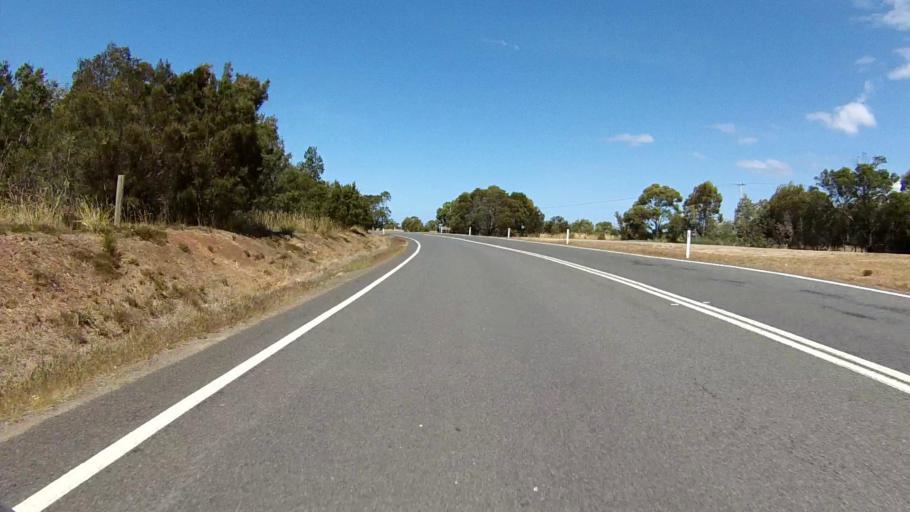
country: AU
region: Tasmania
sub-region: Break O'Day
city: St Helens
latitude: -42.0509
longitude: 148.0529
